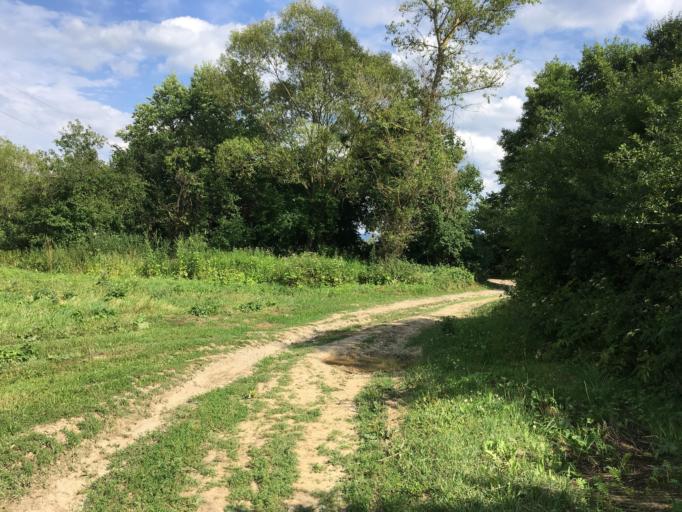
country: SK
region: Trenciansky
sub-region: Okres Povazska Bystrica
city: Povazska Bystrica
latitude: 49.0608
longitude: 18.3887
